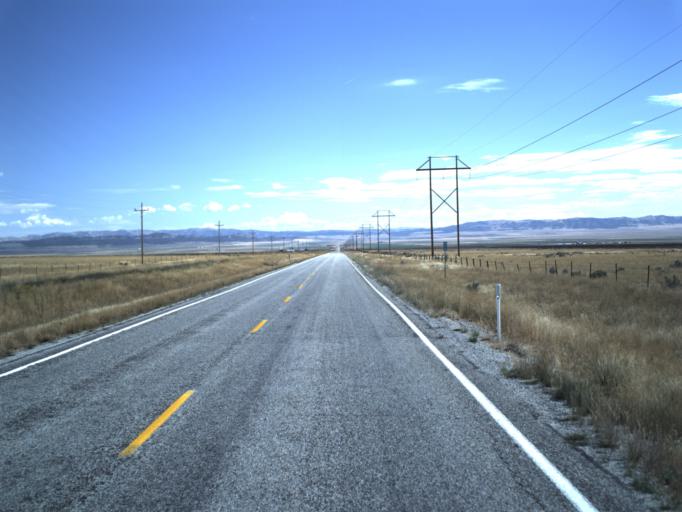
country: US
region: Idaho
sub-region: Oneida County
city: Malad City
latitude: 41.9655
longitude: -113.0363
